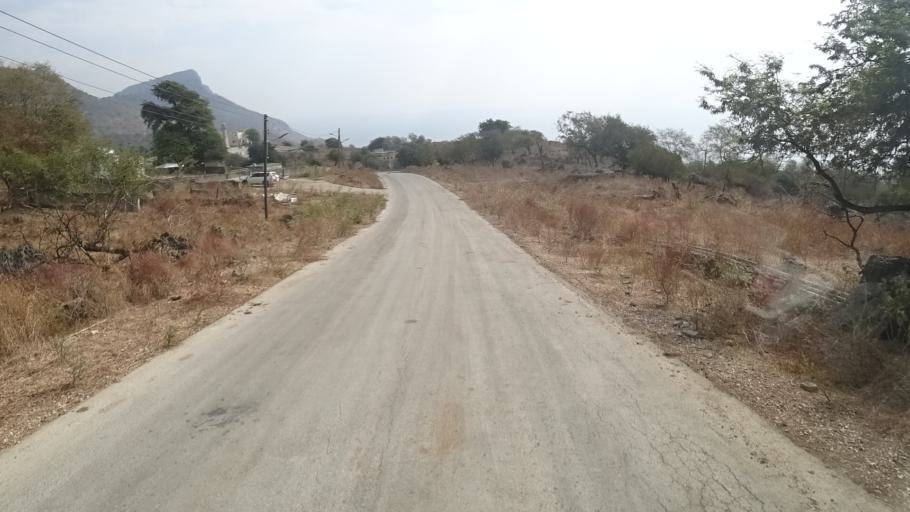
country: YE
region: Al Mahrah
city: Hawf
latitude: 16.7135
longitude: 53.2494
